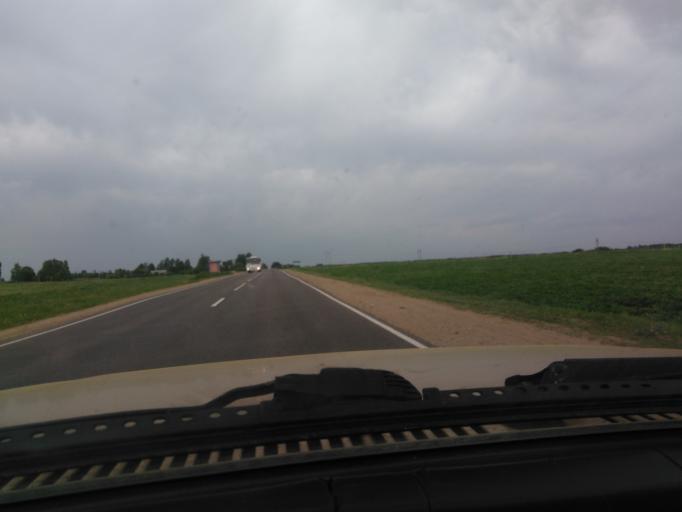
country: BY
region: Mogilev
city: Kamyennyya Lavy
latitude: 54.0511
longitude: 30.3260
